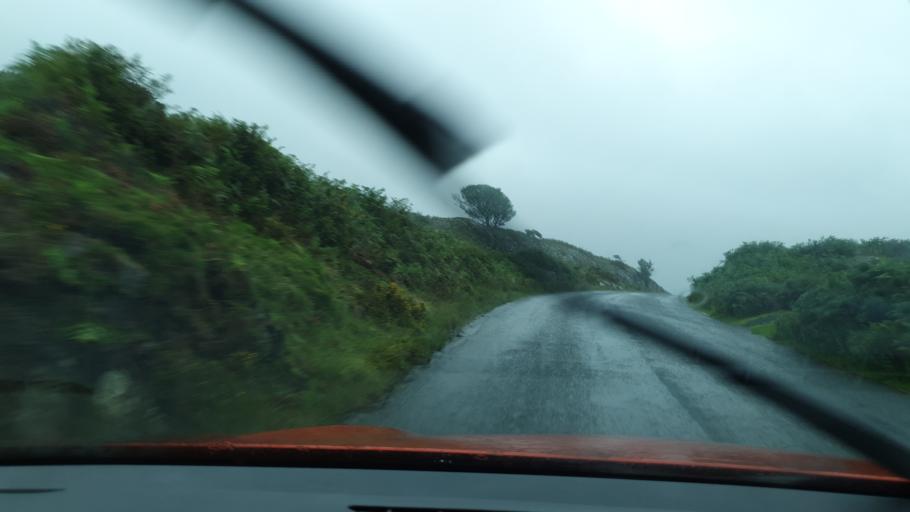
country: GB
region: England
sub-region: Cumbria
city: Millom
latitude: 54.3192
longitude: -3.2339
